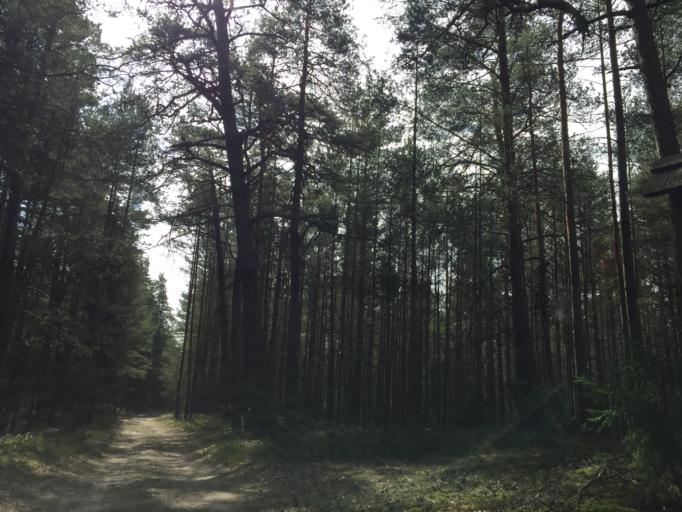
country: LV
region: Salacgrivas
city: Salacgriva
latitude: 57.6947
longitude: 24.3593
